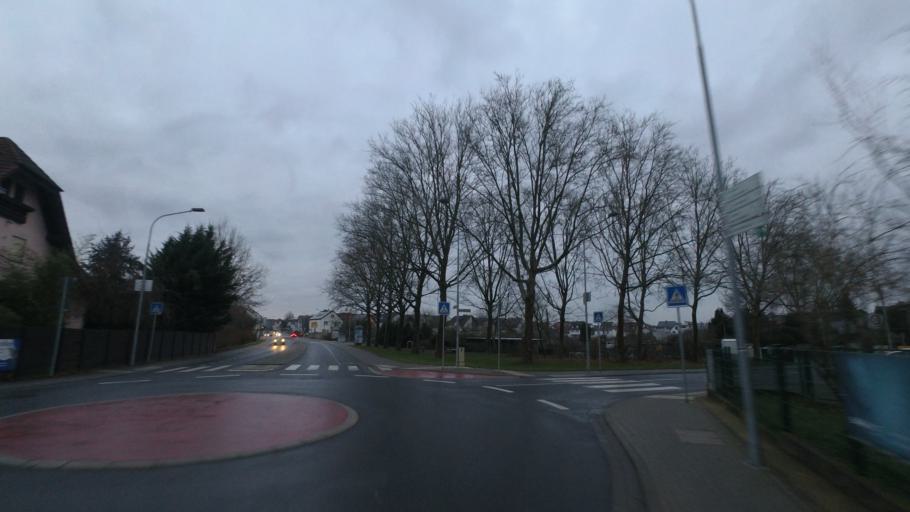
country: DE
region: Hesse
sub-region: Regierungsbezirk Darmstadt
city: Seligenstadt
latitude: 50.0400
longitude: 8.9765
